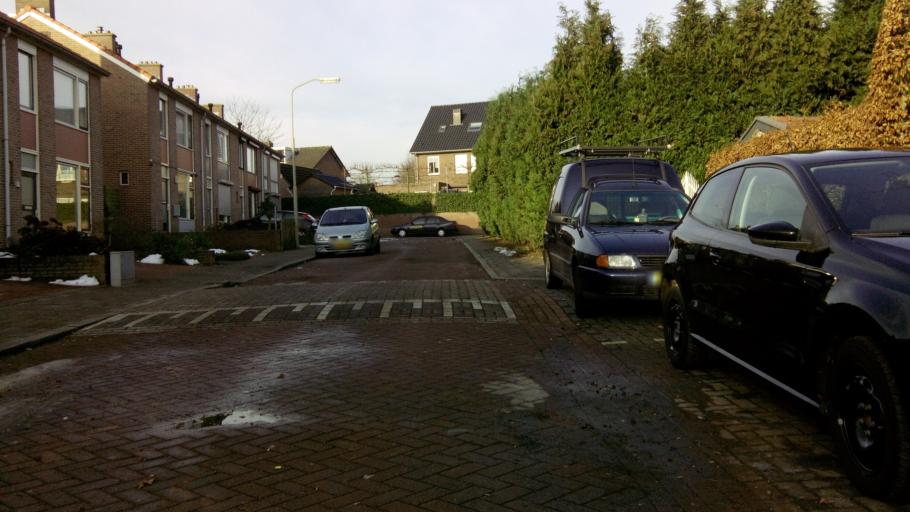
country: NL
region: Gelderland
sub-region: Gemeente Groesbeek
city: Groesbeek
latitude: 51.7868
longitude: 5.9196
